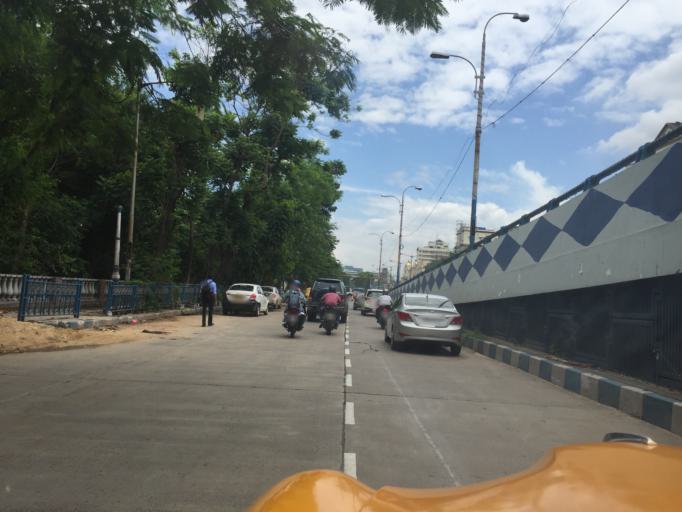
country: IN
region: West Bengal
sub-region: Kolkata
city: Bara Bazar
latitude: 22.5584
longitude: 88.3503
